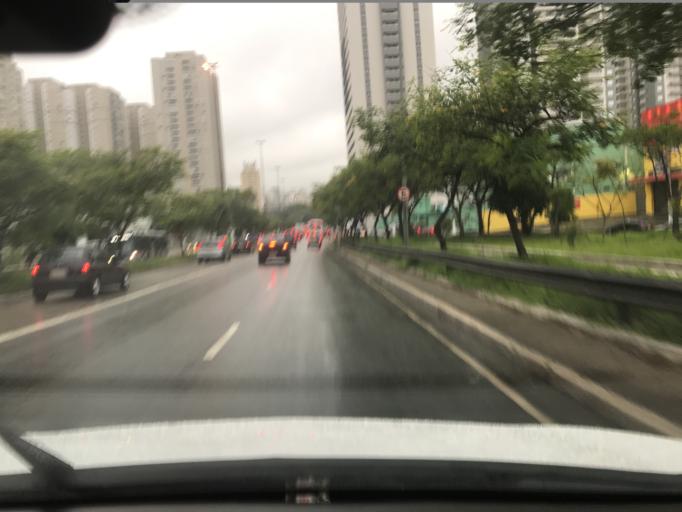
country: BR
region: Sao Paulo
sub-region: Sao Paulo
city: Sao Paulo
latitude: -23.5169
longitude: -46.6671
